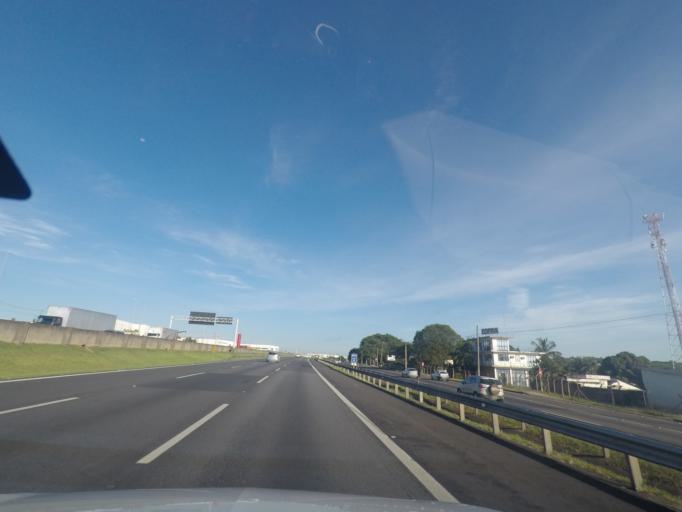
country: BR
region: Sao Paulo
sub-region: Hortolandia
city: Hortolandia
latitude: -22.8141
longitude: -47.2084
